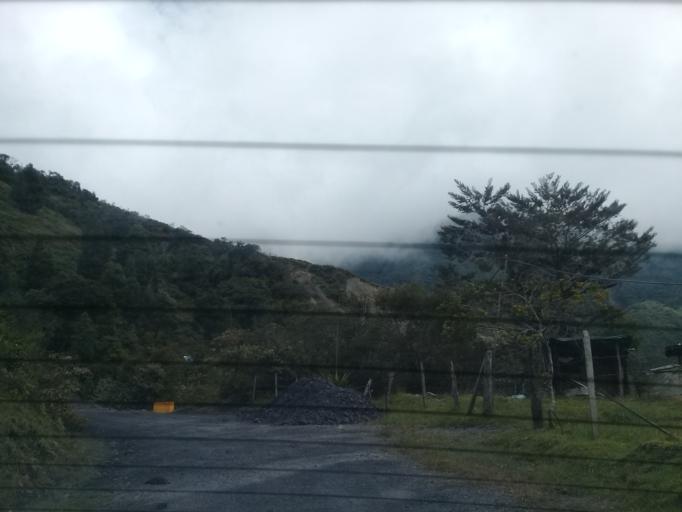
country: CO
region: Cundinamarca
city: Gachala
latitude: 4.7028
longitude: -73.4388
